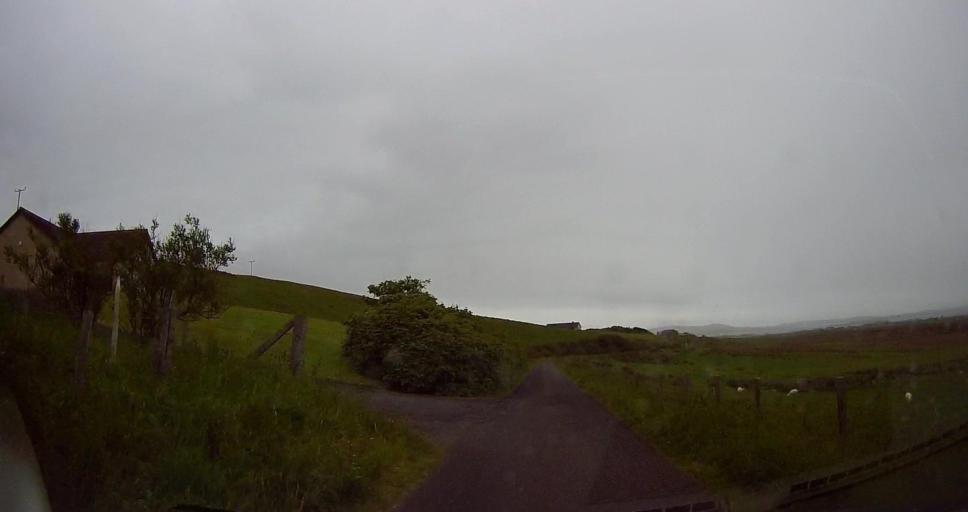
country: GB
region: Scotland
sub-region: Orkney Islands
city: Stromness
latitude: 58.9766
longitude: -3.1616
